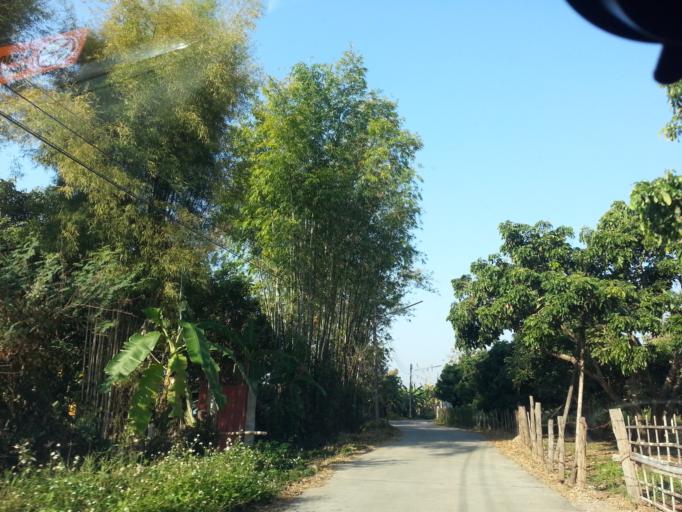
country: TH
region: Chiang Mai
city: San Sai
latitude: 18.8915
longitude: 99.1148
